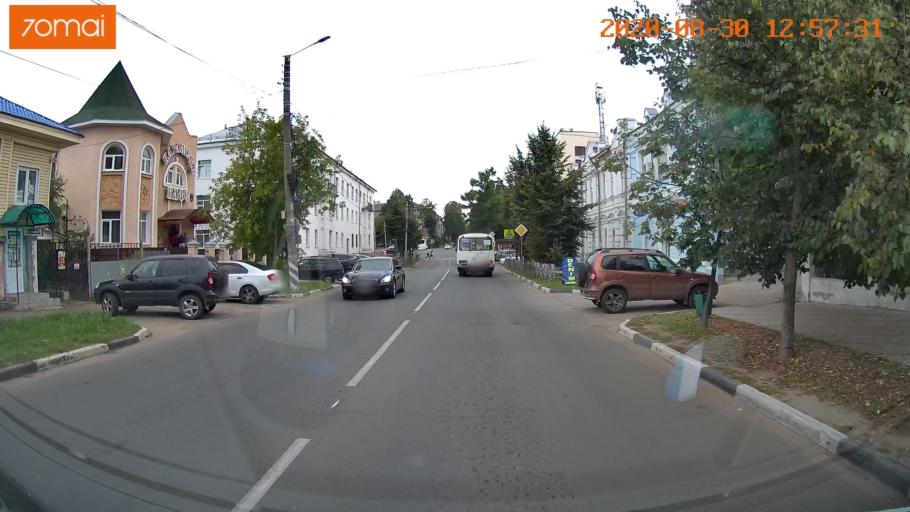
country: RU
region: Ivanovo
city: Kineshma
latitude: 57.4449
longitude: 42.1570
